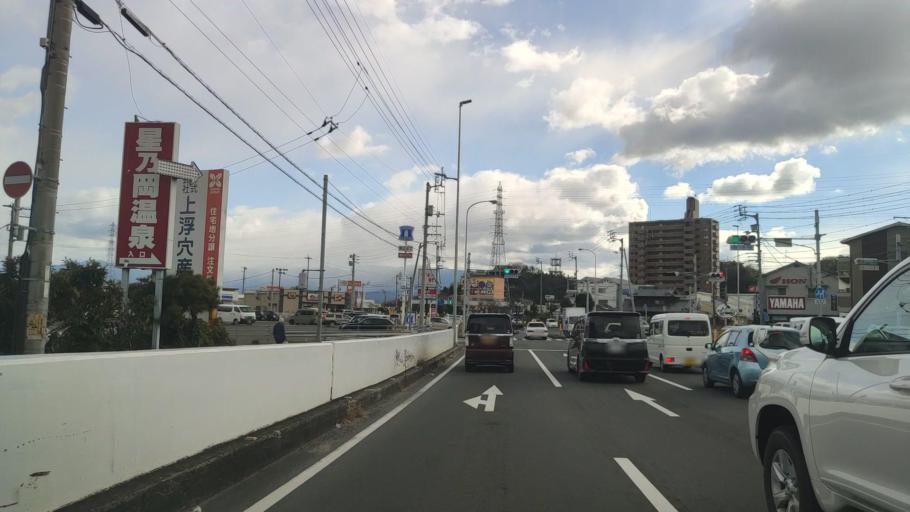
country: JP
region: Ehime
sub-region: Shikoku-chuo Shi
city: Matsuyama
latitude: 33.8222
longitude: 132.7866
